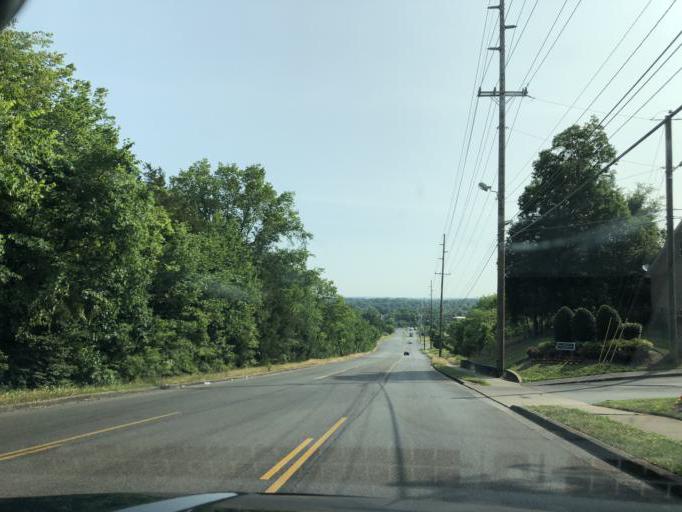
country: US
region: Tennessee
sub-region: Rutherford County
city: La Vergne
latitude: 36.0606
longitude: -86.6329
